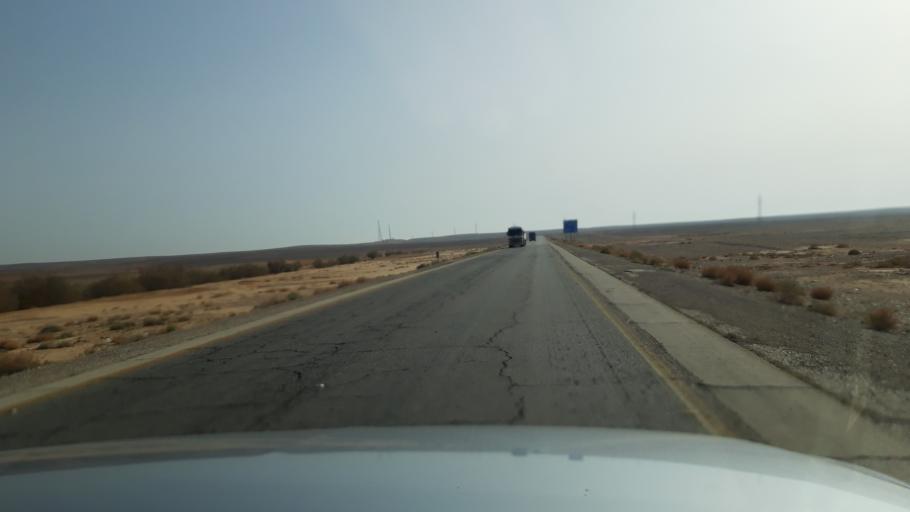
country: JO
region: Amman
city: Al Azraq ash Shamali
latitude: 31.7309
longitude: 36.4974
